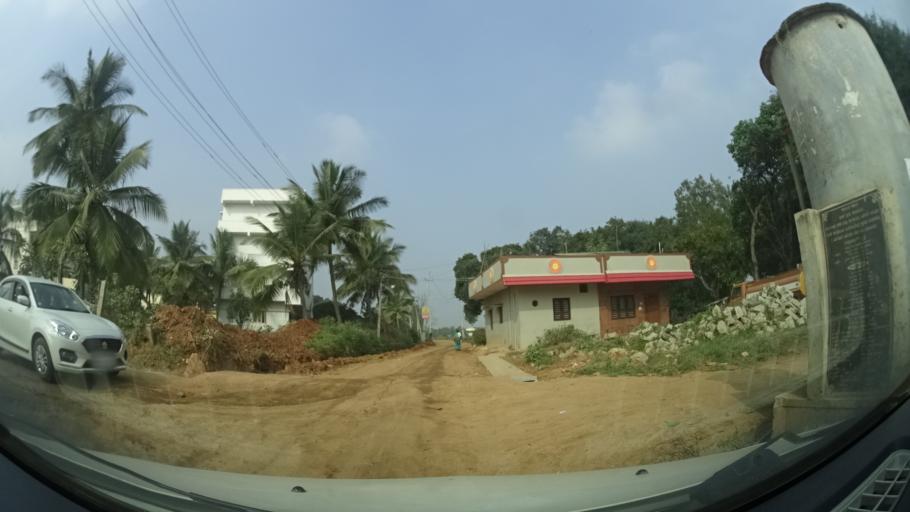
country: IN
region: Karnataka
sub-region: Bangalore Urban
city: Anekal
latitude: 12.7933
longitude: 77.6503
